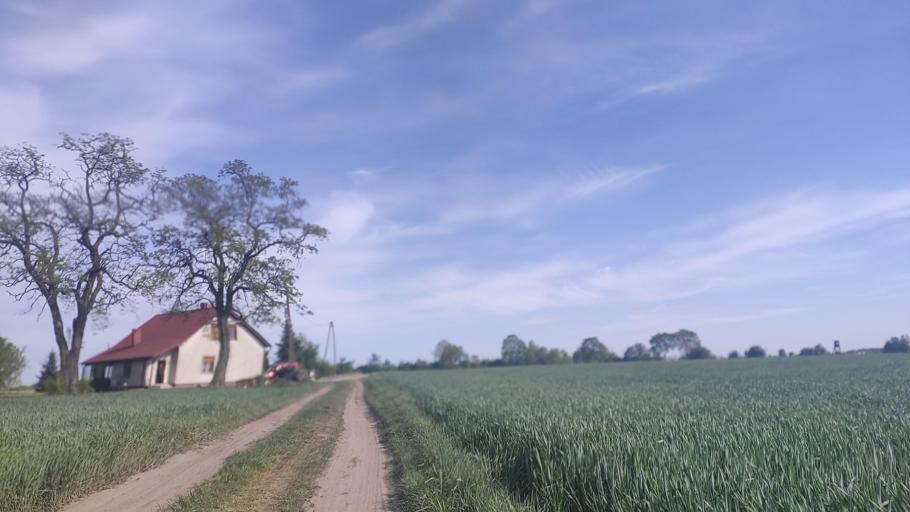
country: PL
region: Greater Poland Voivodeship
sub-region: Powiat poznanski
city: Swarzedz
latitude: 52.4146
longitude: 17.1516
